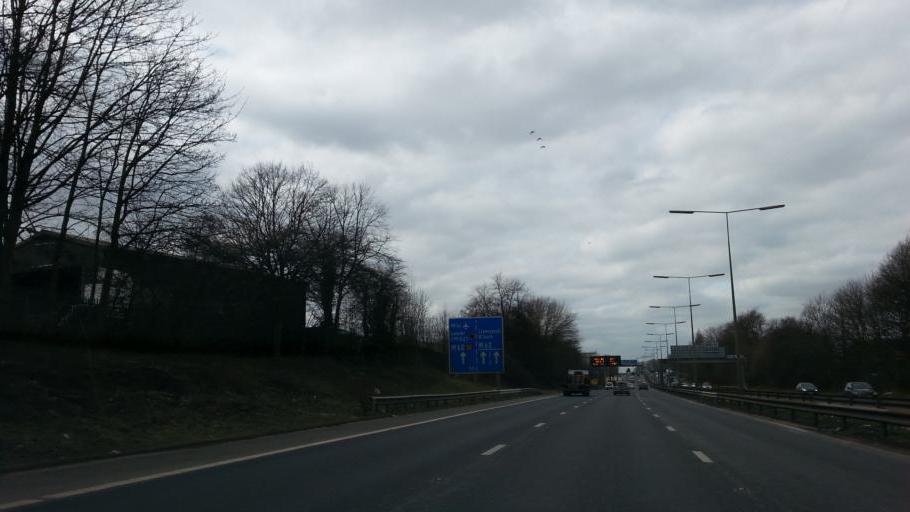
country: GB
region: England
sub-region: Manchester
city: Swinton
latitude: 53.4870
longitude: -2.3480
